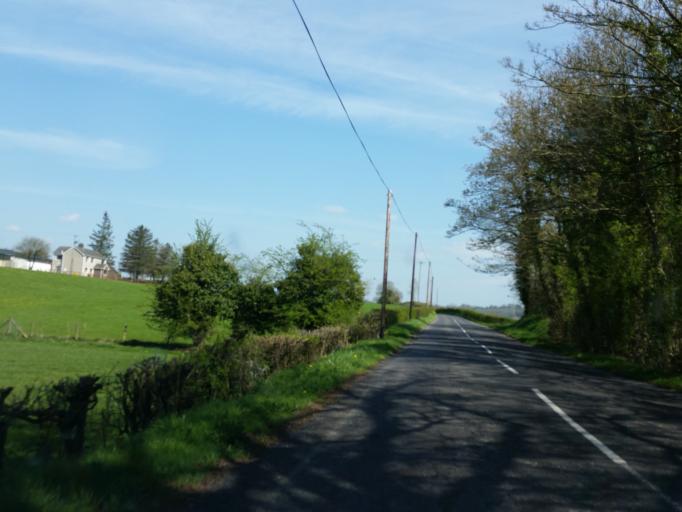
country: GB
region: Northern Ireland
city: Lisnaskea
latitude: 54.2934
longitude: -7.4222
